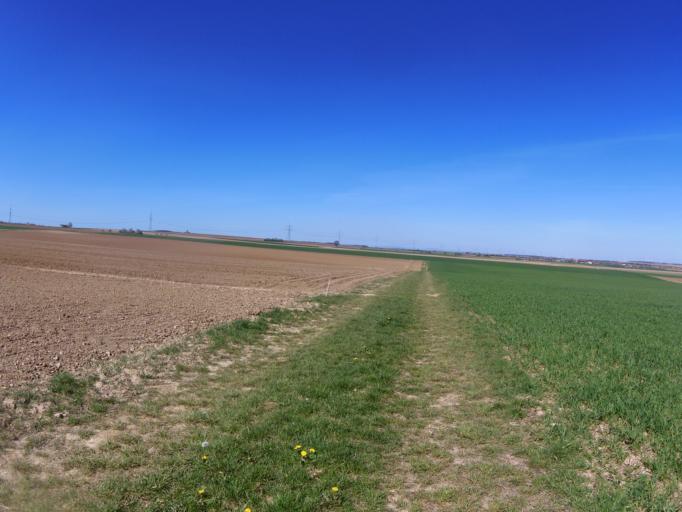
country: DE
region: Bavaria
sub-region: Regierungsbezirk Unterfranken
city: Biebelried
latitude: 49.8020
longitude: 10.0922
